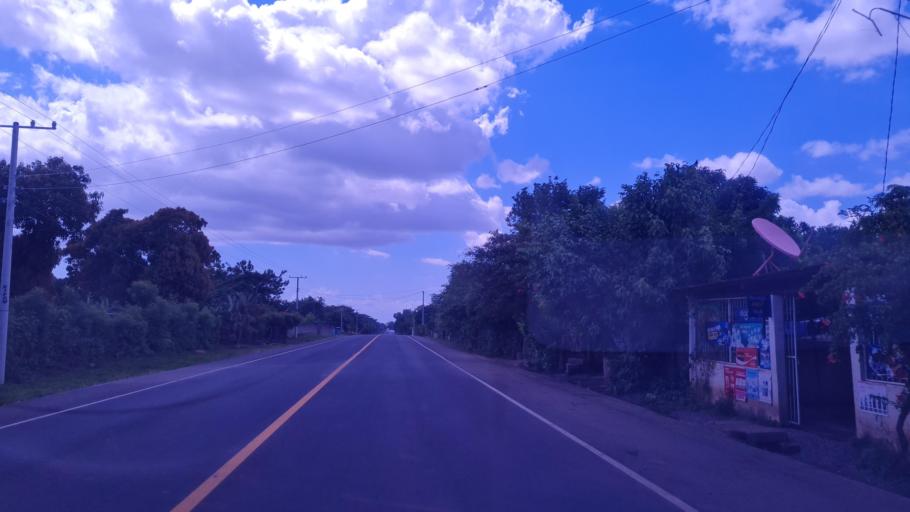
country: NI
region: Masaya
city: Nindiri
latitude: 12.0244
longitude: -86.1206
